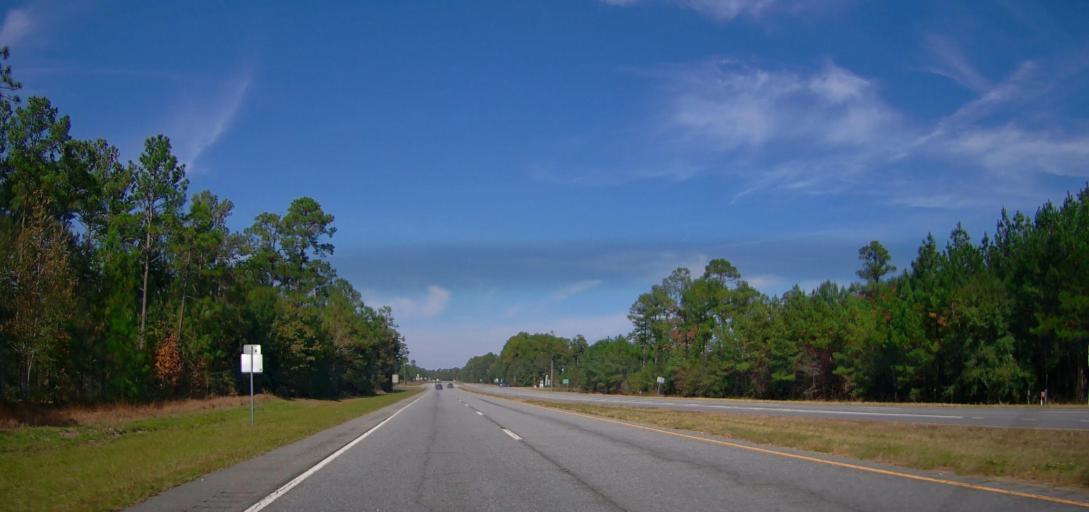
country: US
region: Georgia
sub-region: Lee County
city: Leesburg
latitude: 31.7241
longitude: -83.9877
